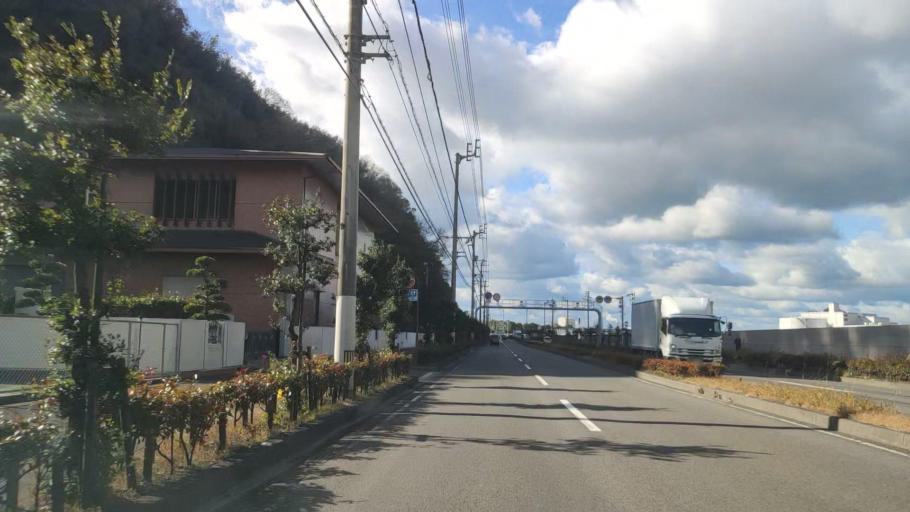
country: JP
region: Ehime
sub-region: Shikoku-chuo Shi
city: Matsuyama
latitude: 33.8467
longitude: 132.7114
